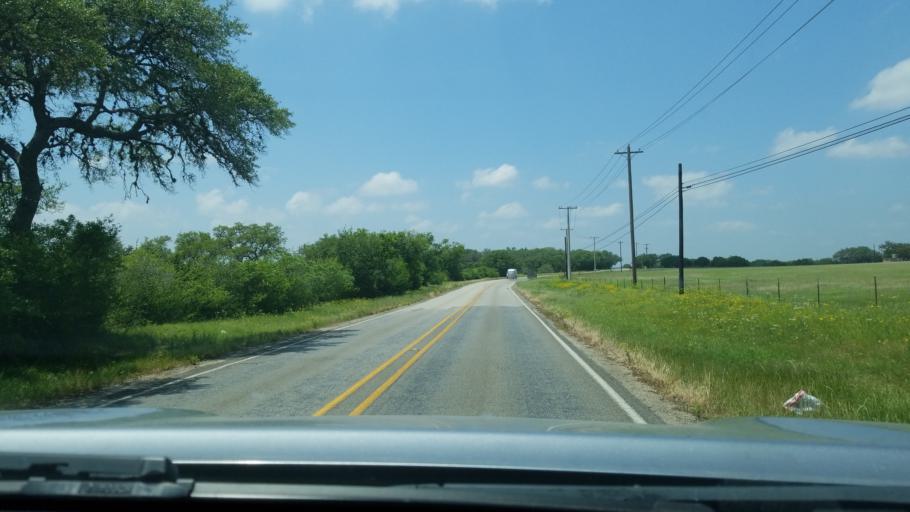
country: US
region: Texas
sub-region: Hays County
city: Woodcreek
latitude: 30.0251
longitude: -98.1634
